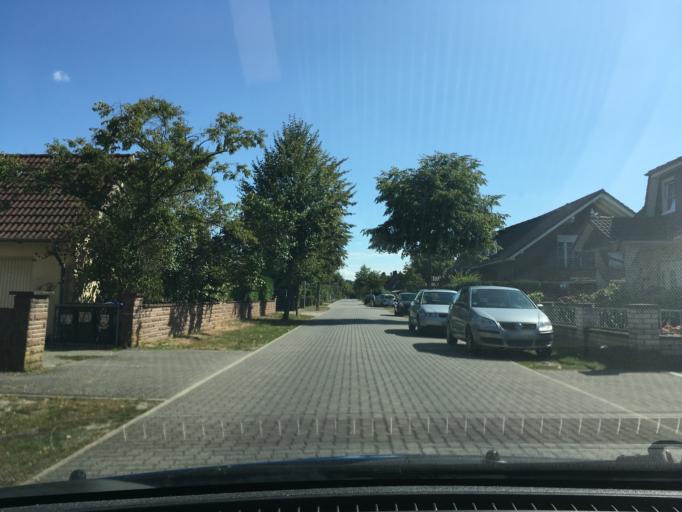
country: DE
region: Lower Saxony
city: Winsen (Aller)
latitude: 52.6705
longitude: 9.9071
